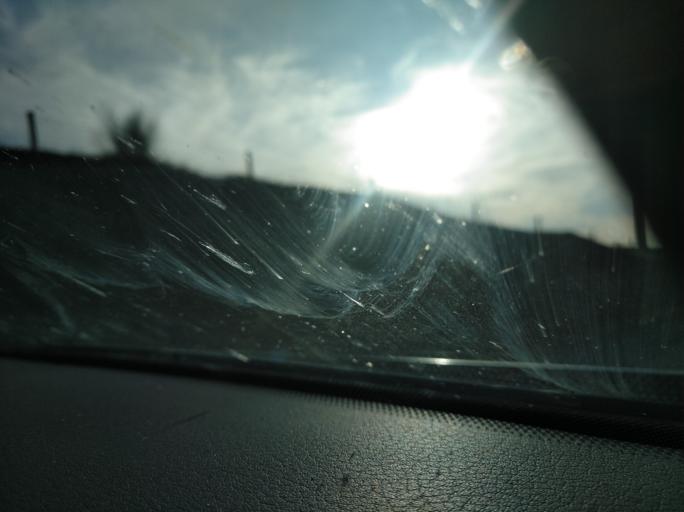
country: PT
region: Evora
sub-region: Estremoz
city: Estremoz
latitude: 38.9549
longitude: -7.5389
